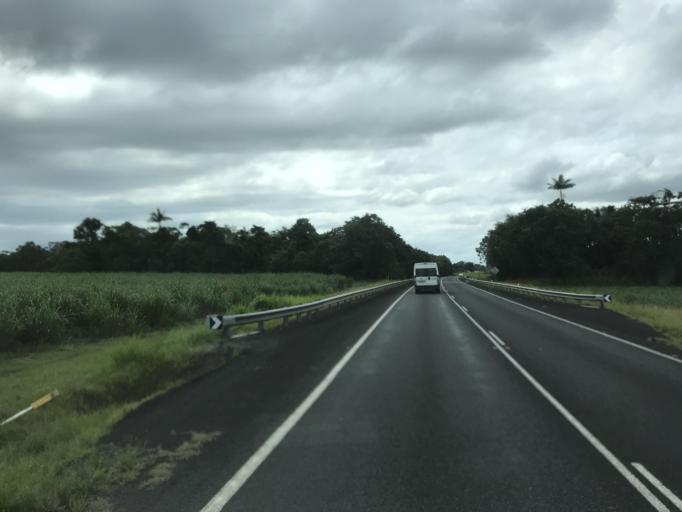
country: AU
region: Queensland
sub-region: Cassowary Coast
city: Innisfail
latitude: -17.6482
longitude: 146.0320
